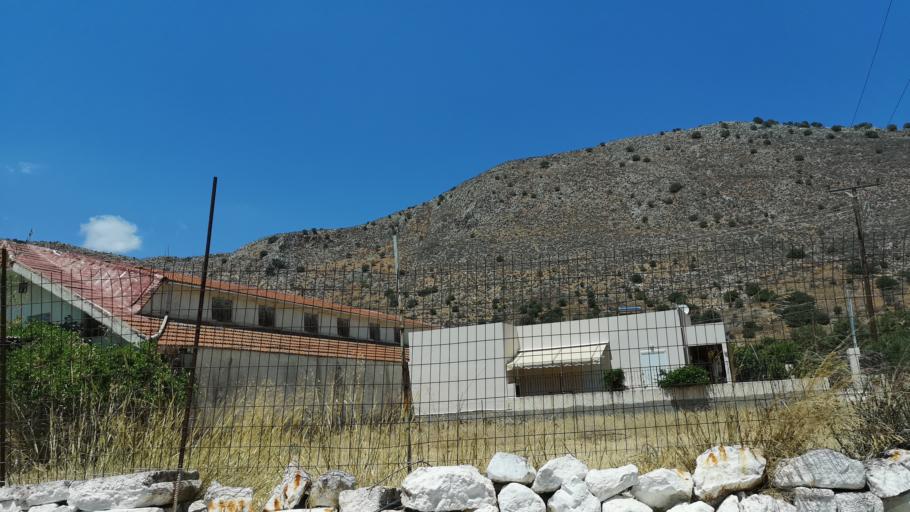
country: GR
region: Crete
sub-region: Nomos Lasithiou
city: Neapoli
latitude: 35.2456
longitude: 25.6398
